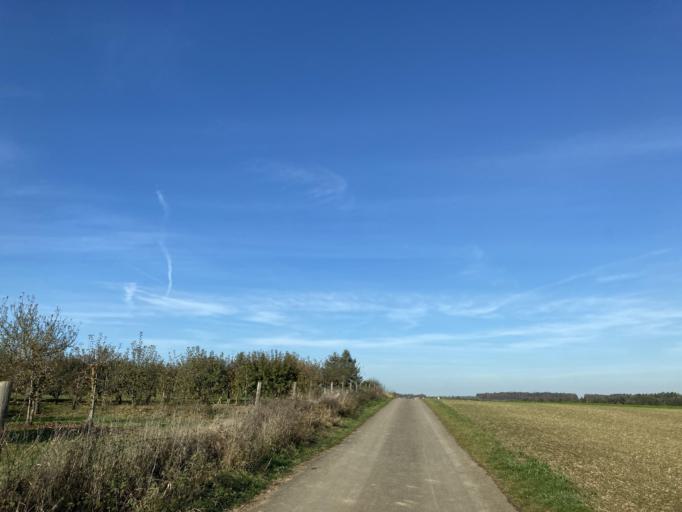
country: DE
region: Baden-Wuerttemberg
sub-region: Tuebingen Region
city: Rottenburg
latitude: 48.4895
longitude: 8.8839
